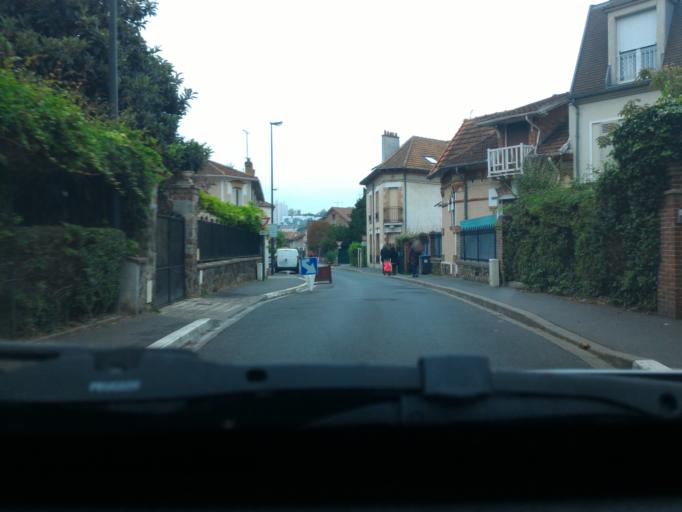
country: FR
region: Ile-de-France
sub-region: Departement des Hauts-de-Seine
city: Bourg-la-Reine
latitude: 48.7809
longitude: 2.3112
